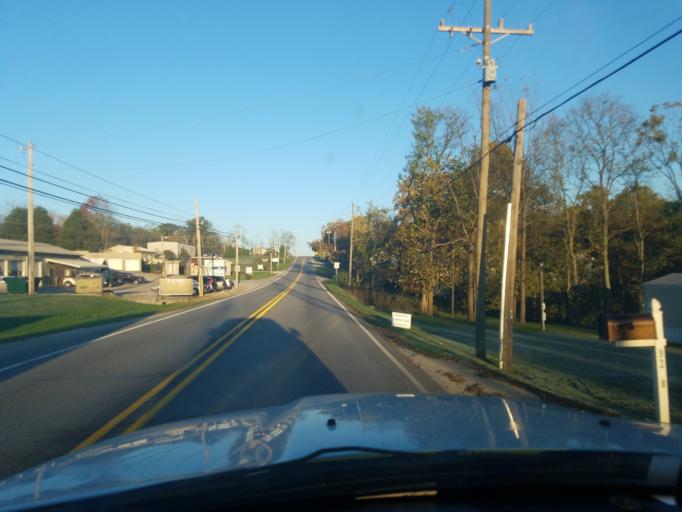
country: US
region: Indiana
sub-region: Floyd County
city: Galena
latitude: 38.3698
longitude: -85.9801
